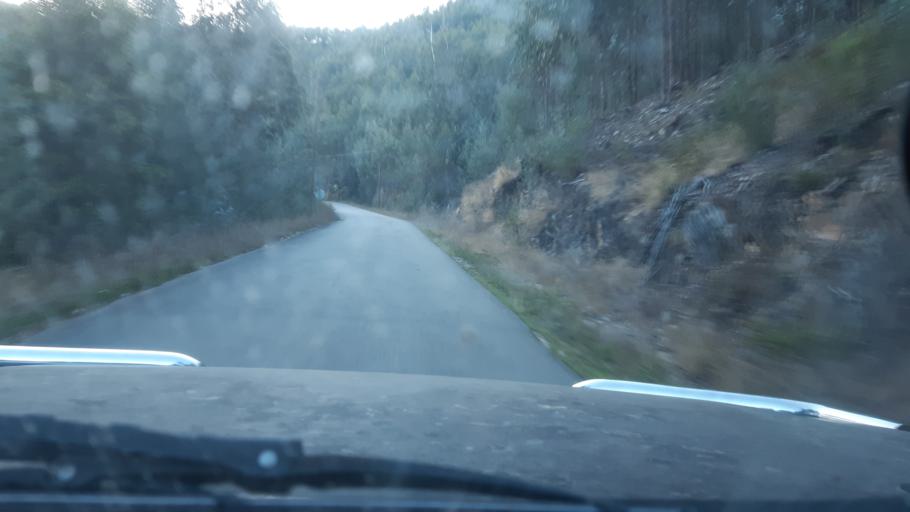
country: PT
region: Aveiro
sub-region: Agueda
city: Aguada de Cima
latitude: 40.5683
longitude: -8.3580
